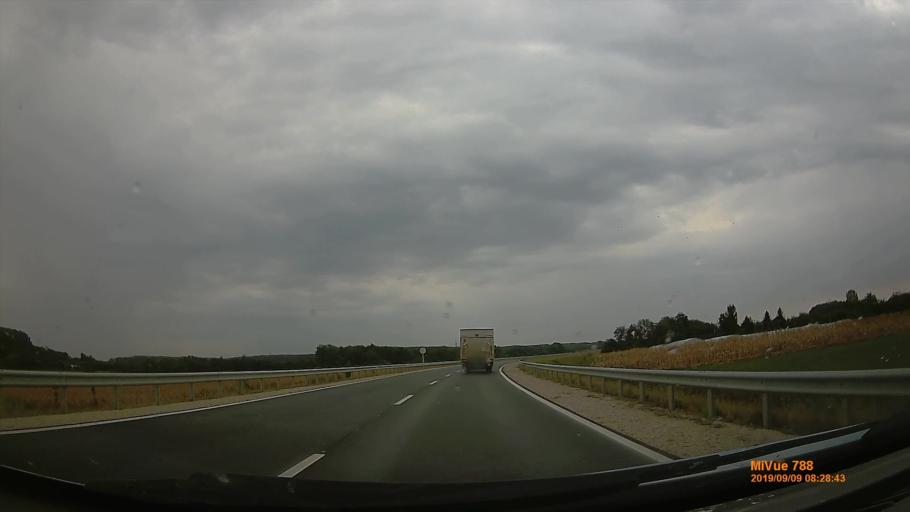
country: HU
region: Szabolcs-Szatmar-Bereg
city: Kalmanhaza
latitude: 47.9227
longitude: 21.6435
